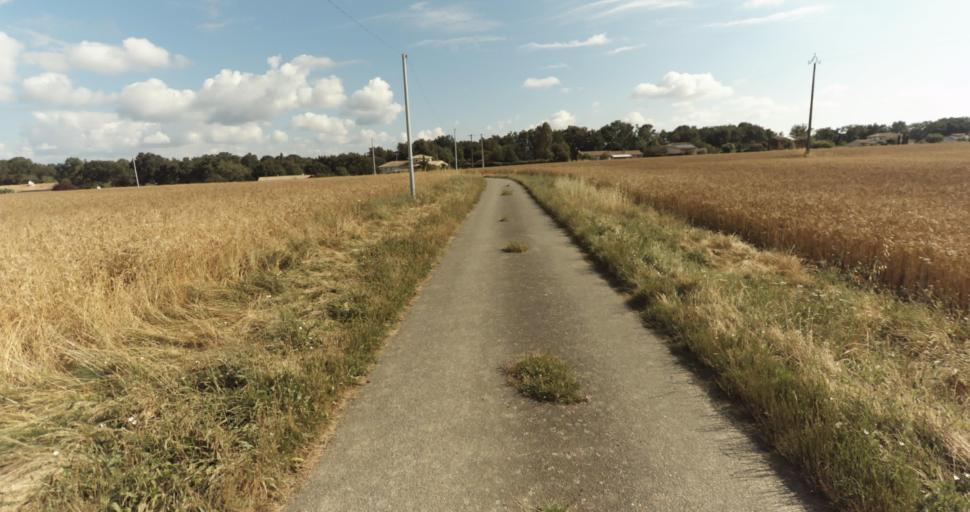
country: FR
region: Midi-Pyrenees
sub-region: Departement de la Haute-Garonne
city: Fonsorbes
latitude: 43.5609
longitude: 1.2205
